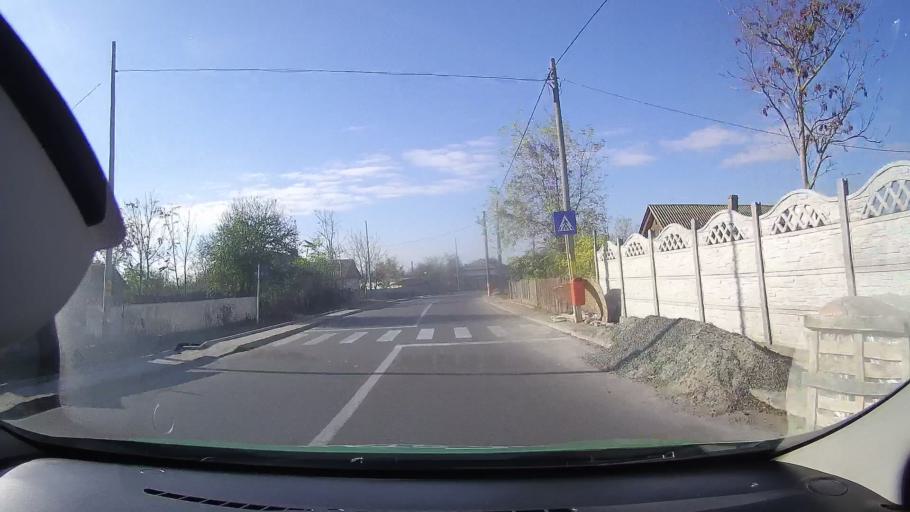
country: RO
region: Tulcea
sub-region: Comuna Murighiol
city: Murighiol
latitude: 45.0215
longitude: 29.1268
